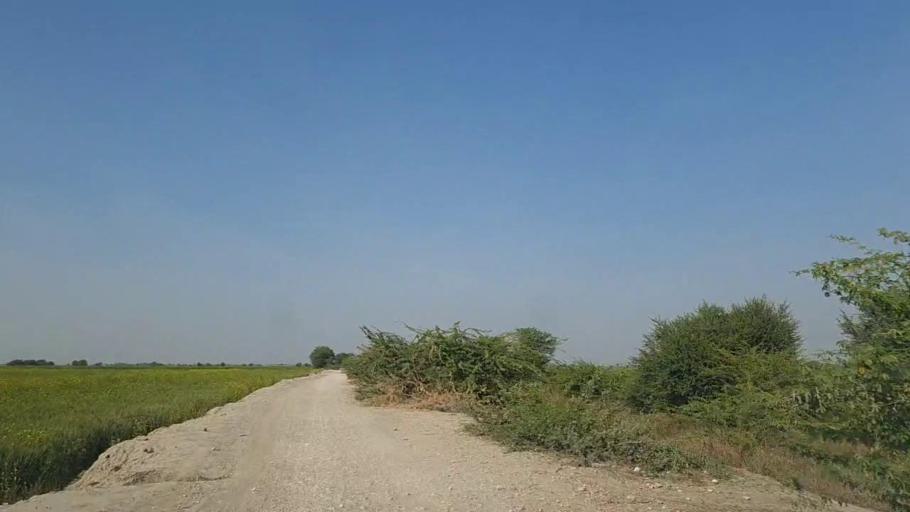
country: PK
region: Sindh
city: Naukot
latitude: 24.9259
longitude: 69.4878
